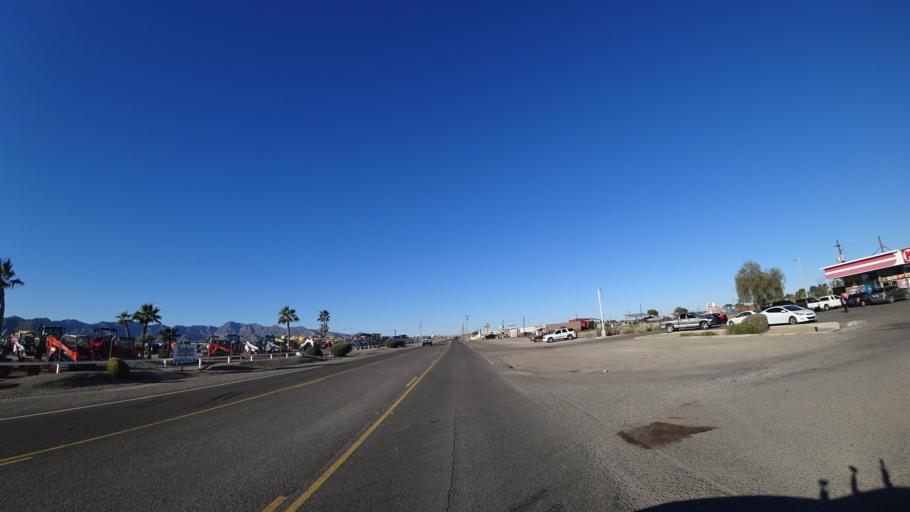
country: US
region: Arizona
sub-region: Maricopa County
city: Citrus Park
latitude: 33.4552
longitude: -112.4788
